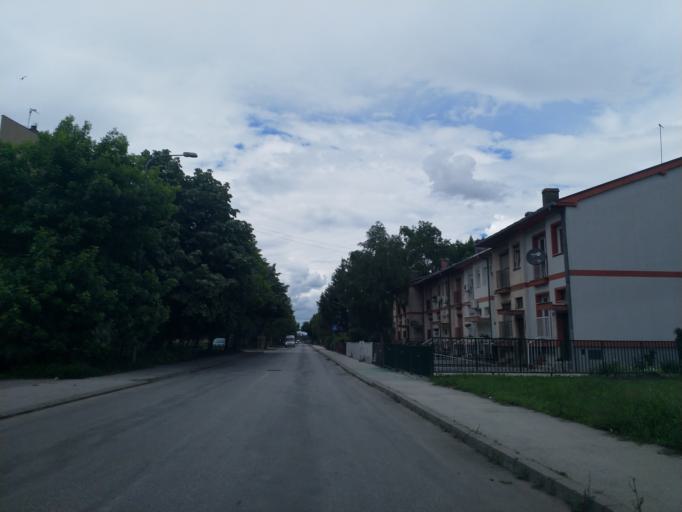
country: RS
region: Central Serbia
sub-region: Pomoravski Okrug
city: Jagodina
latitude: 43.9674
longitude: 21.2765
